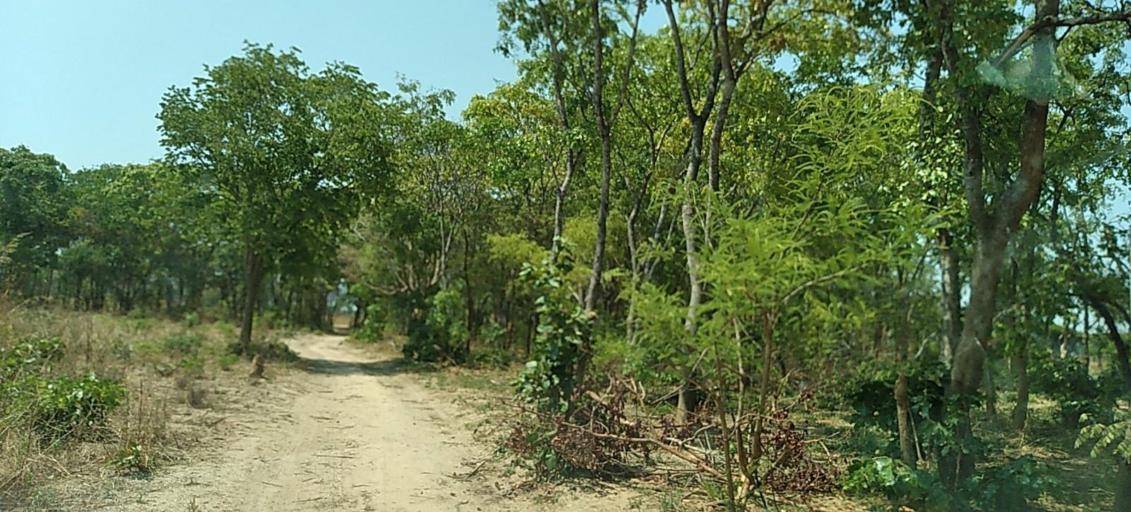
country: ZM
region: Copperbelt
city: Mpongwe
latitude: -13.8662
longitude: 28.0538
